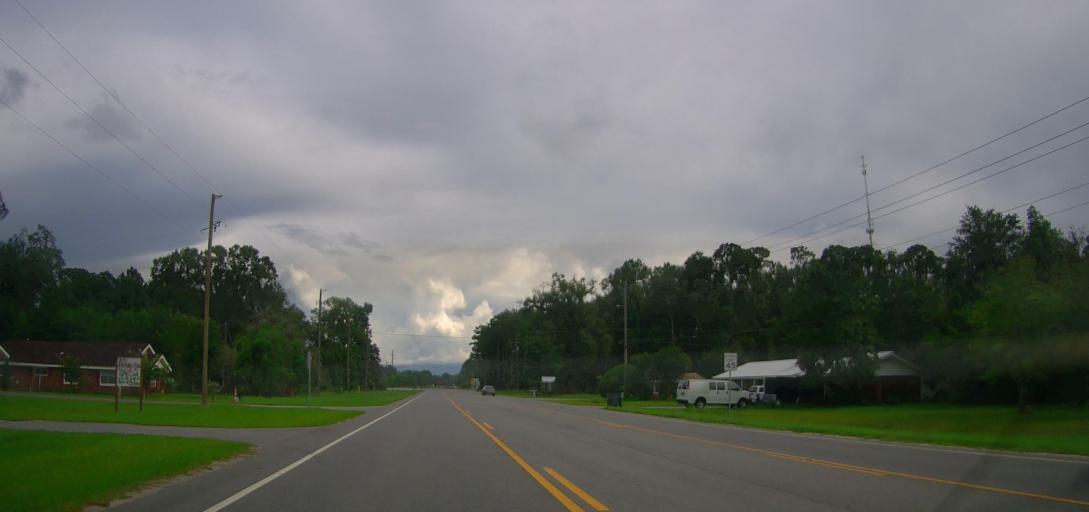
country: US
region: Georgia
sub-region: Wayne County
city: Jesup
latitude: 31.6261
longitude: -81.8991
